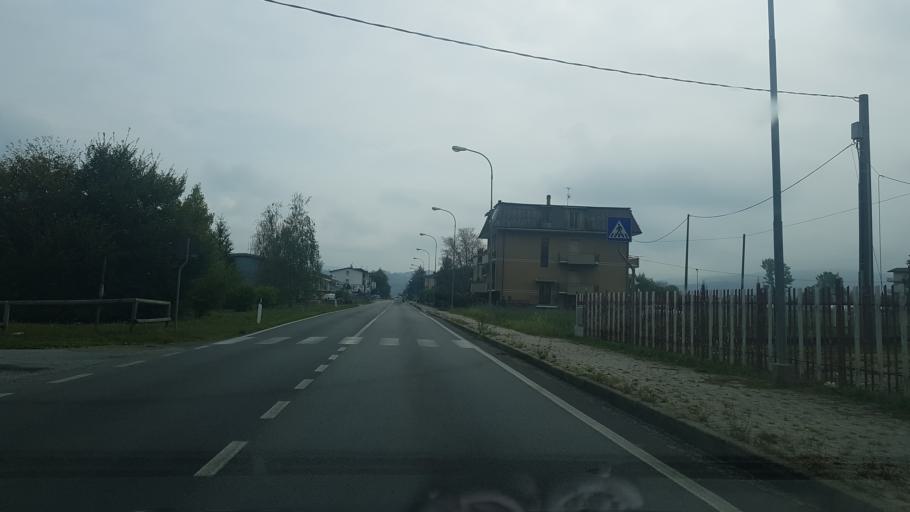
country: IT
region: Piedmont
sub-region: Provincia di Cuneo
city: Ceva
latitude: 44.3869
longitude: 8.0145
